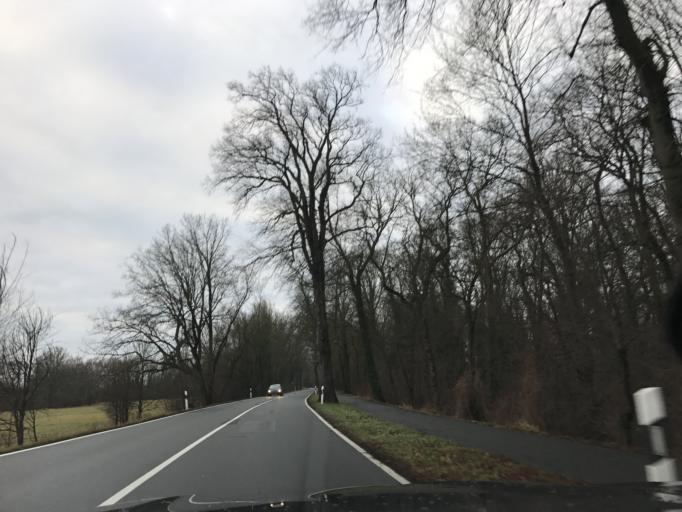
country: DE
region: Brandenburg
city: Werder
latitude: 52.3729
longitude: 12.9583
